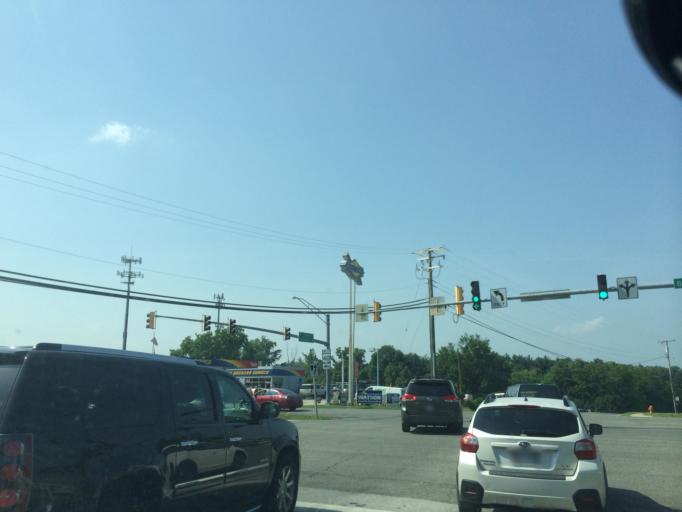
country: US
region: Maryland
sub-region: Howard County
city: Columbia
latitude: 39.2796
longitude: -76.8647
